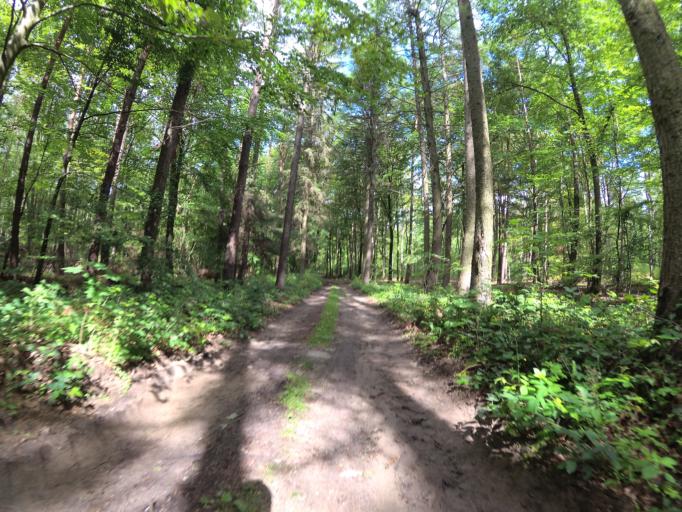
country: PL
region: Pomeranian Voivodeship
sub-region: Powiat wejherowski
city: Bojano
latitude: 54.5054
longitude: 18.4199
